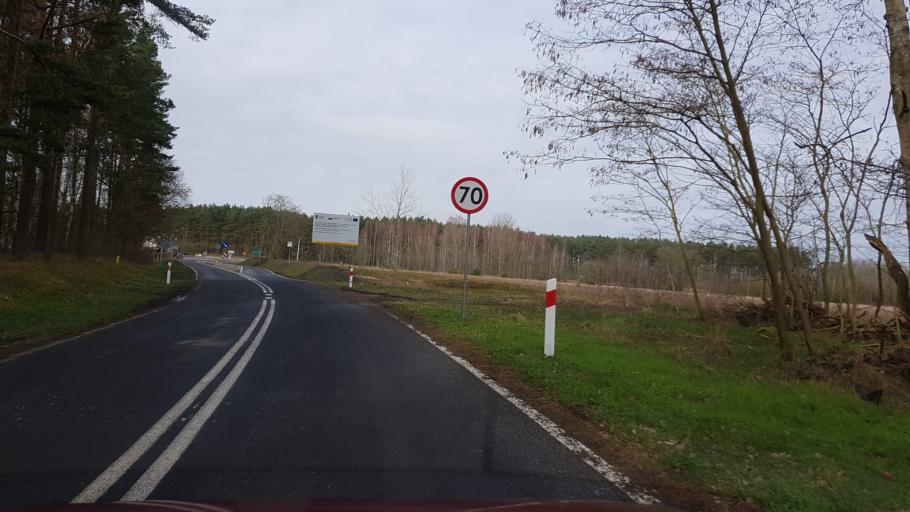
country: PL
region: West Pomeranian Voivodeship
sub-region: Powiat policki
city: Nowe Warpno
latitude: 53.6877
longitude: 14.3560
